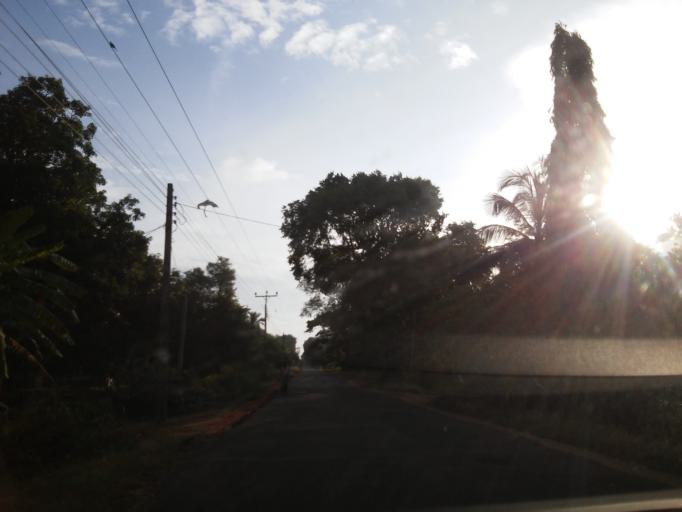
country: LK
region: Central
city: Sigiriya
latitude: 8.1372
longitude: 80.6360
